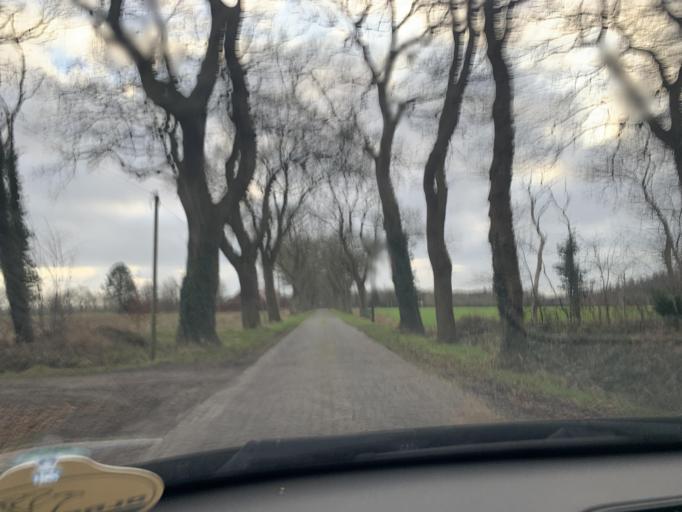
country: DE
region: Lower Saxony
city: Westerstede
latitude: 53.2966
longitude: 7.9292
